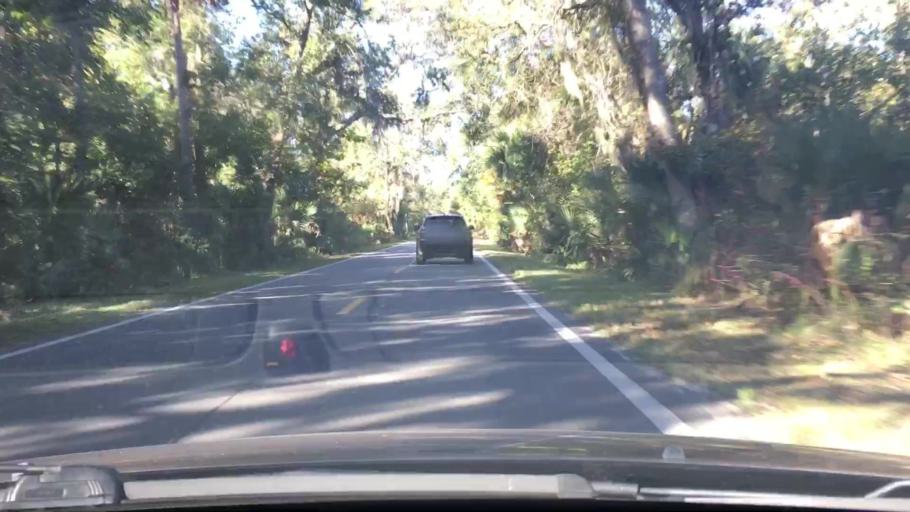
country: US
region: Florida
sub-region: Volusia County
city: Ormond-by-the-Sea
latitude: 29.3823
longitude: -81.1305
